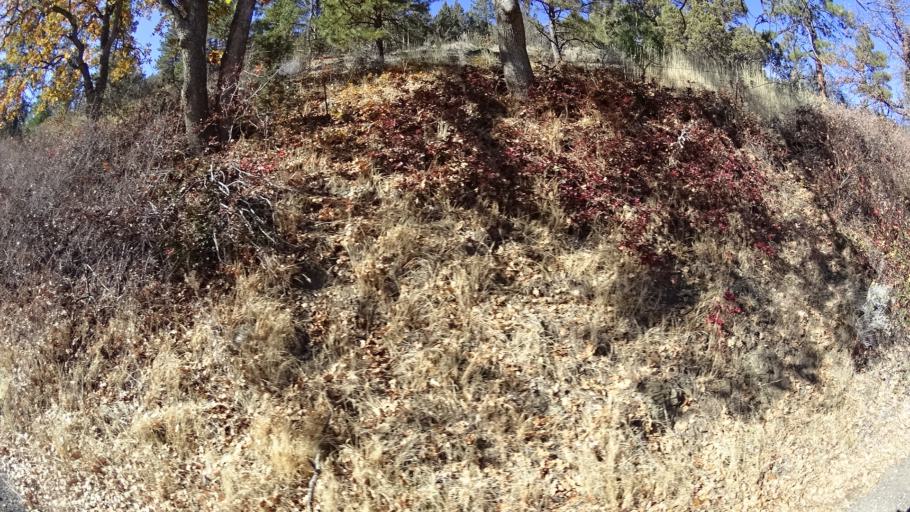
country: US
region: California
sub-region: Siskiyou County
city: Weed
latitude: 41.4807
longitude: -122.5727
